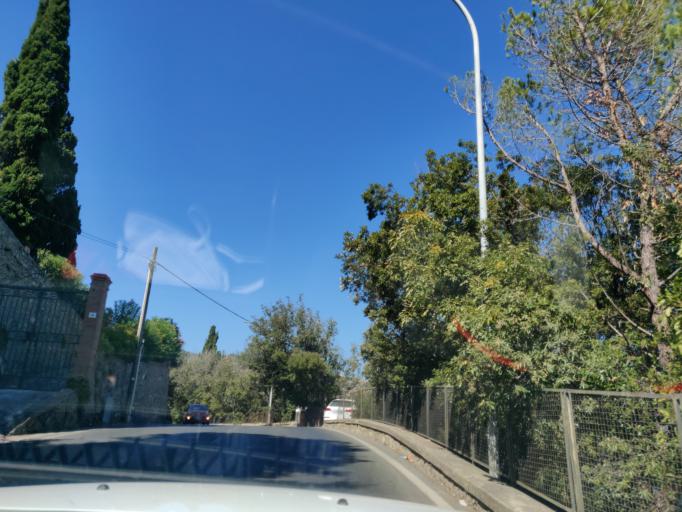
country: IT
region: Tuscany
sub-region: Provincia di Grosseto
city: Monte Argentario
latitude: 42.4368
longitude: 11.1281
